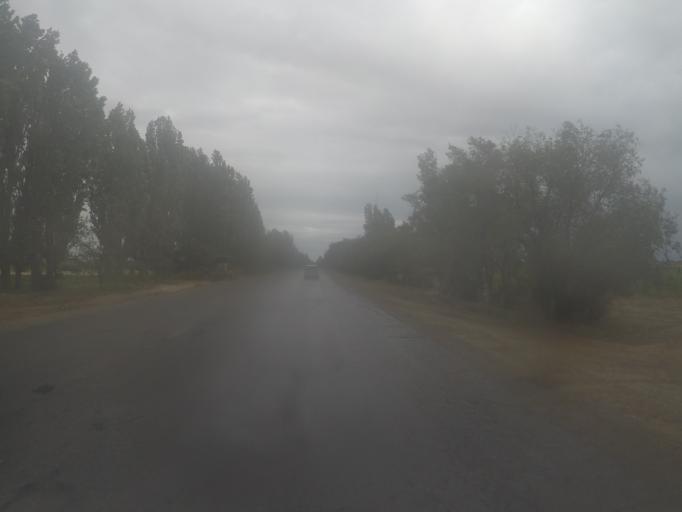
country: KG
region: Ysyk-Koel
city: Balykchy
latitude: 42.4929
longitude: 76.3349
